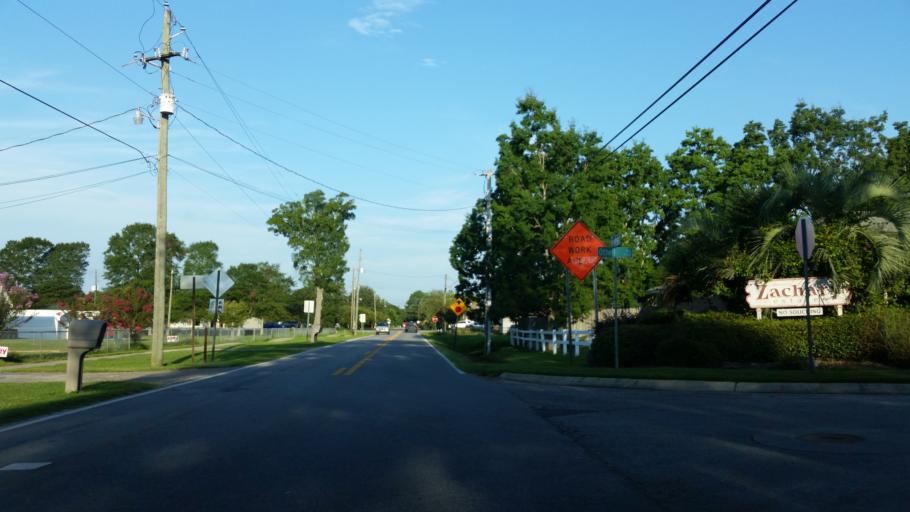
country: US
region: Florida
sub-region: Escambia County
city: Bellview
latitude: 30.4689
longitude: -87.3224
